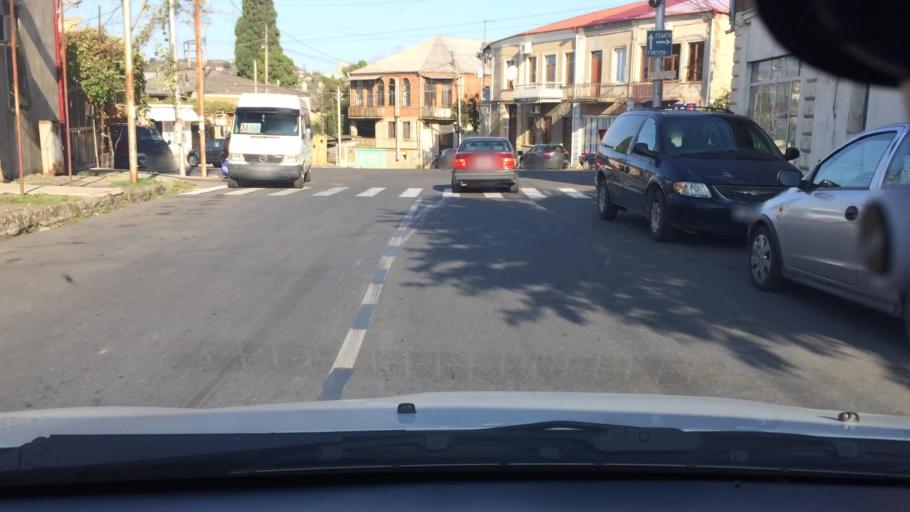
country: GE
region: Imereti
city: Kutaisi
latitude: 42.2721
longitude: 42.7121
